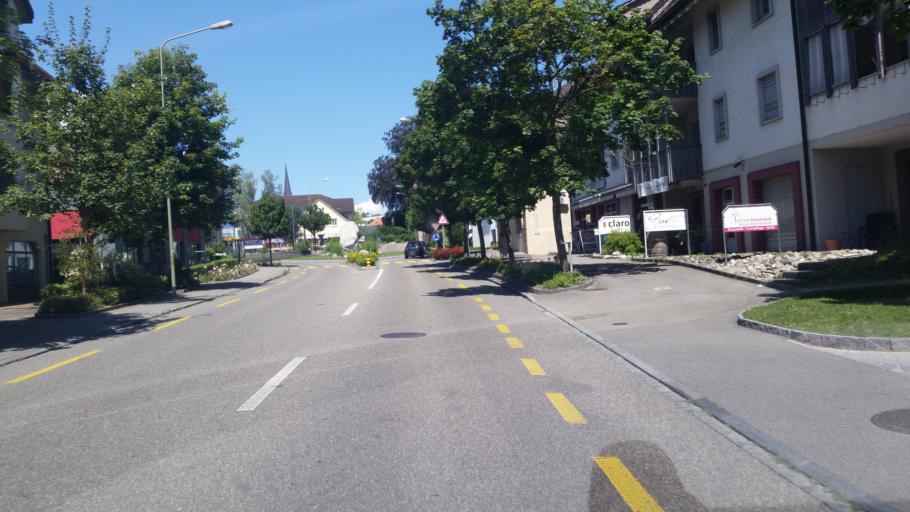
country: CH
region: Zurich
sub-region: Bezirk Buelach
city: Bulach
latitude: 47.5176
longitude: 8.5388
